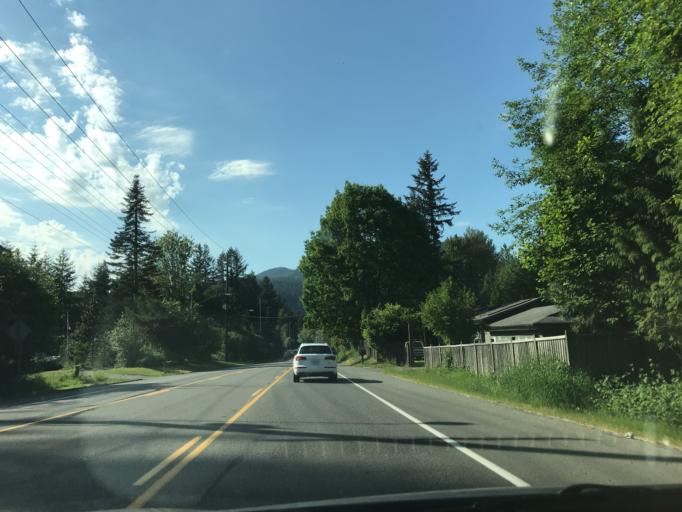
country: US
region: Washington
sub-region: King County
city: Mirrormont
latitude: 47.4739
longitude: -122.0246
